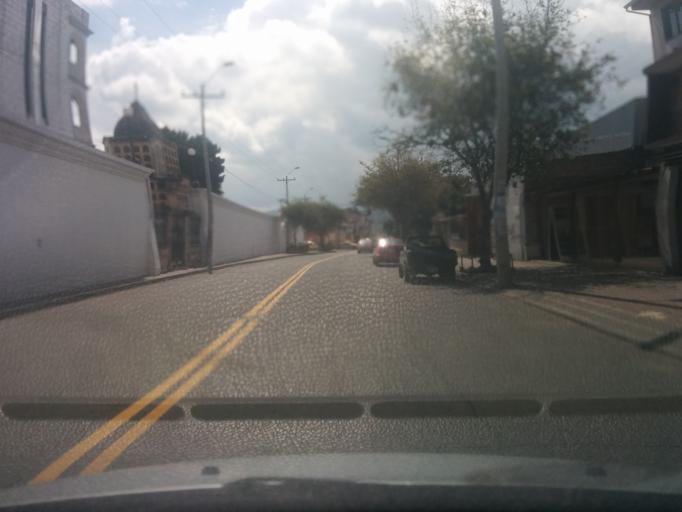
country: EC
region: Azuay
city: Cuenca
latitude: -2.8989
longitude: -78.9912
